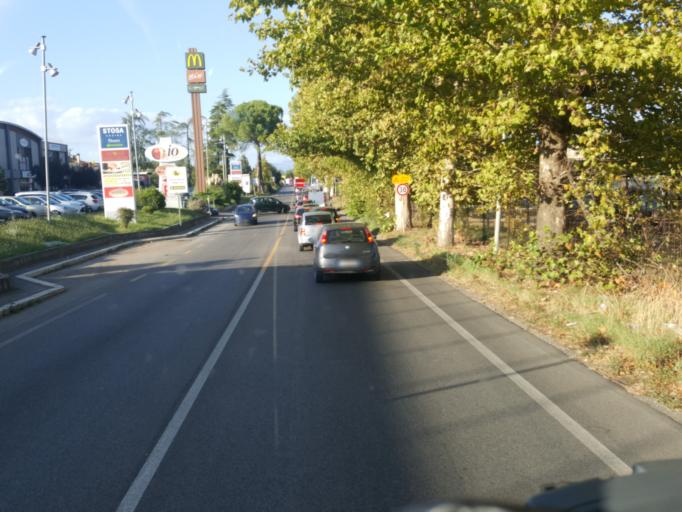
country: IT
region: Latium
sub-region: Citta metropolitana di Roma Capitale
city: Bivio di Capanelle
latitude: 42.1142
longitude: 12.5871
